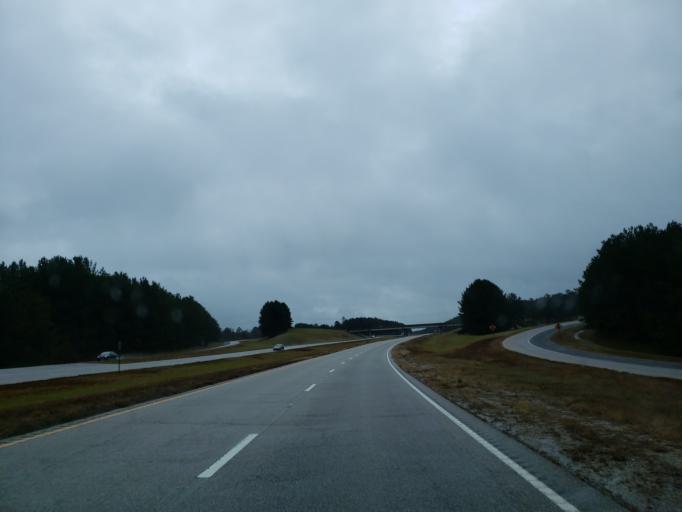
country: US
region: Mississippi
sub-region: Lauderdale County
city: Meridian
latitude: 32.2993
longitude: -88.6932
